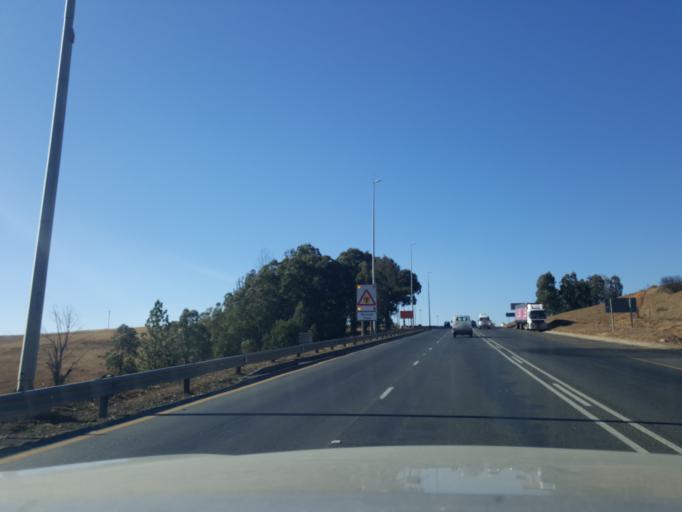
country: ZA
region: Mpumalanga
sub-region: Nkangala District Municipality
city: Belfast
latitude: -25.6316
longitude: 30.2554
